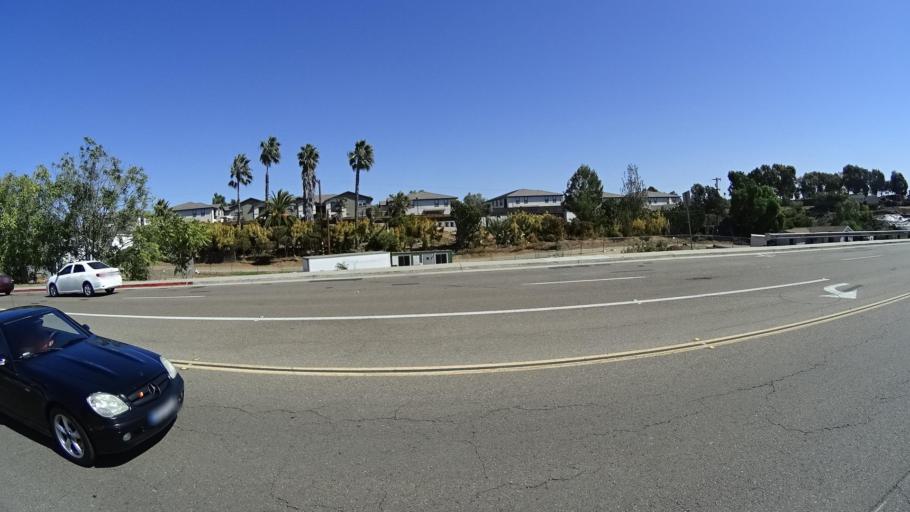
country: US
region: California
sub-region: San Diego County
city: National City
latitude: 32.6660
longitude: -117.0760
